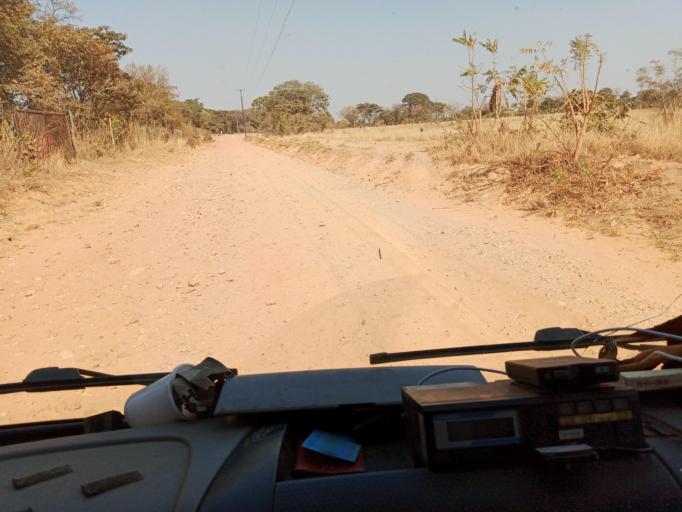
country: ZM
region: Lusaka
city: Lusaka
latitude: -15.3387
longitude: 28.1922
